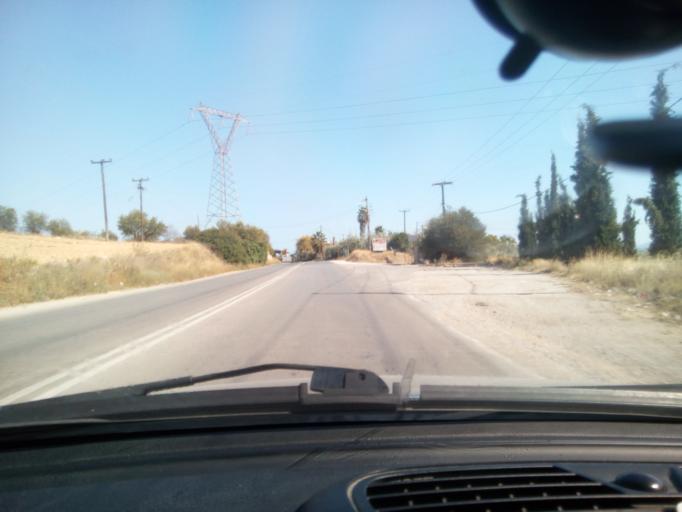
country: GR
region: Central Greece
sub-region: Nomos Evvoias
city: Vasilikon
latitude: 38.4184
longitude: 23.6858
